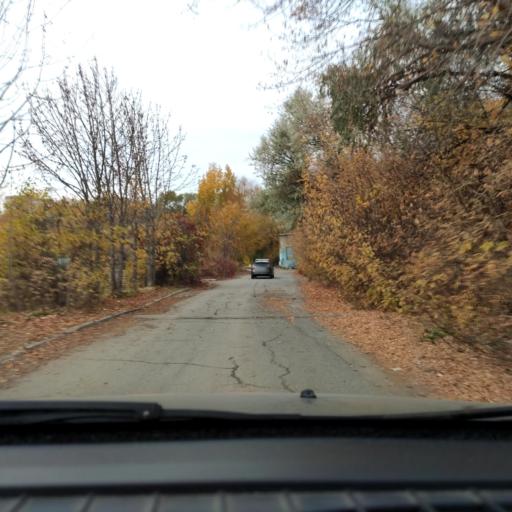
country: RU
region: Samara
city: Tol'yatti
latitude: 53.4980
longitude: 49.2625
